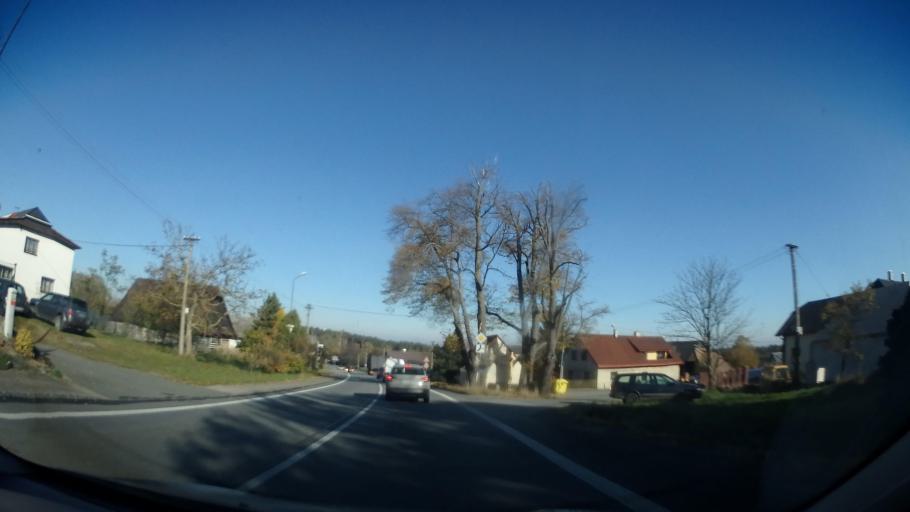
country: CZ
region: Pardubicky
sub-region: Okres Chrudim
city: Nasavrky
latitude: 49.8261
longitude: 15.8210
